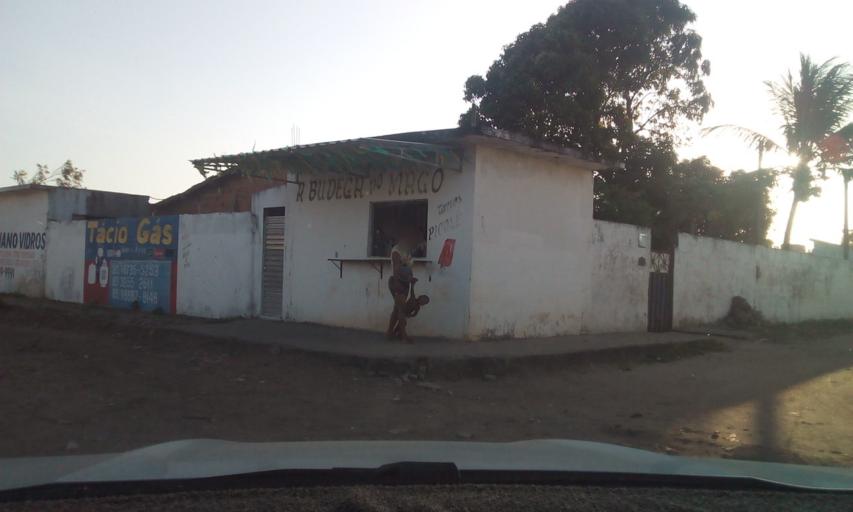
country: BR
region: Paraiba
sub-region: Bayeux
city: Bayeux
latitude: -7.1809
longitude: -34.9313
